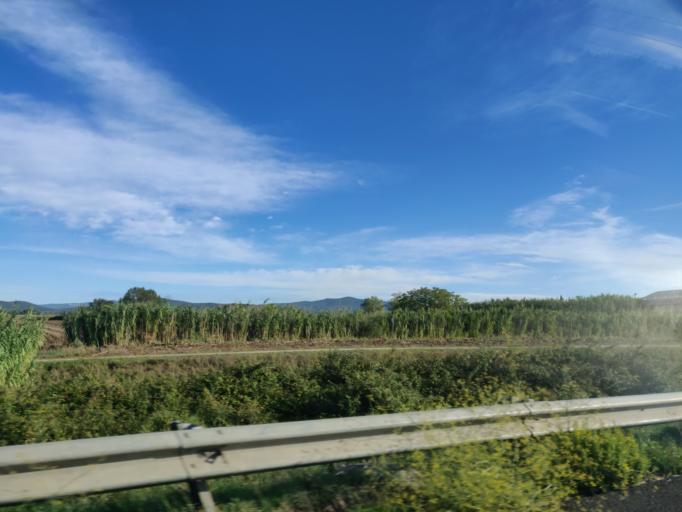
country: IT
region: Tuscany
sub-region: Provincia di Grosseto
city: Grosseto
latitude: 42.7959
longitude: 11.1107
